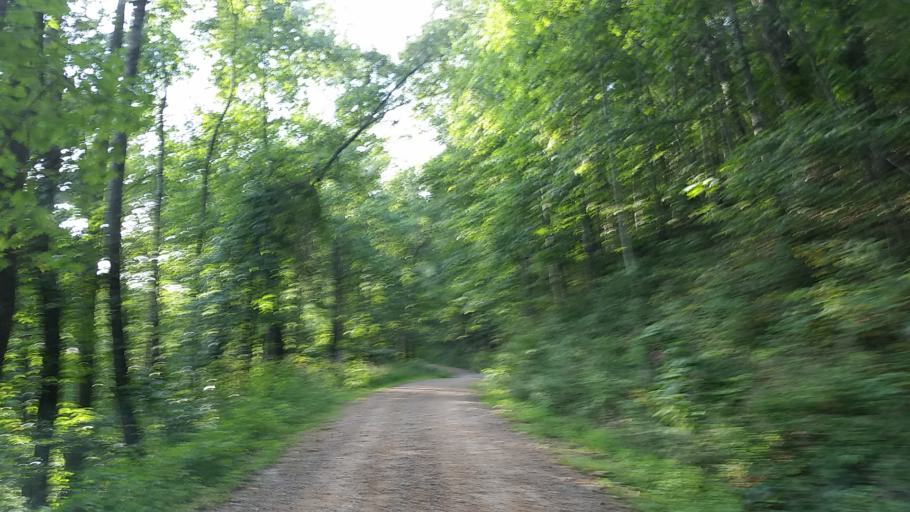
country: US
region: Georgia
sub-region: Lumpkin County
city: Dahlonega
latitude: 34.6508
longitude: -84.0803
